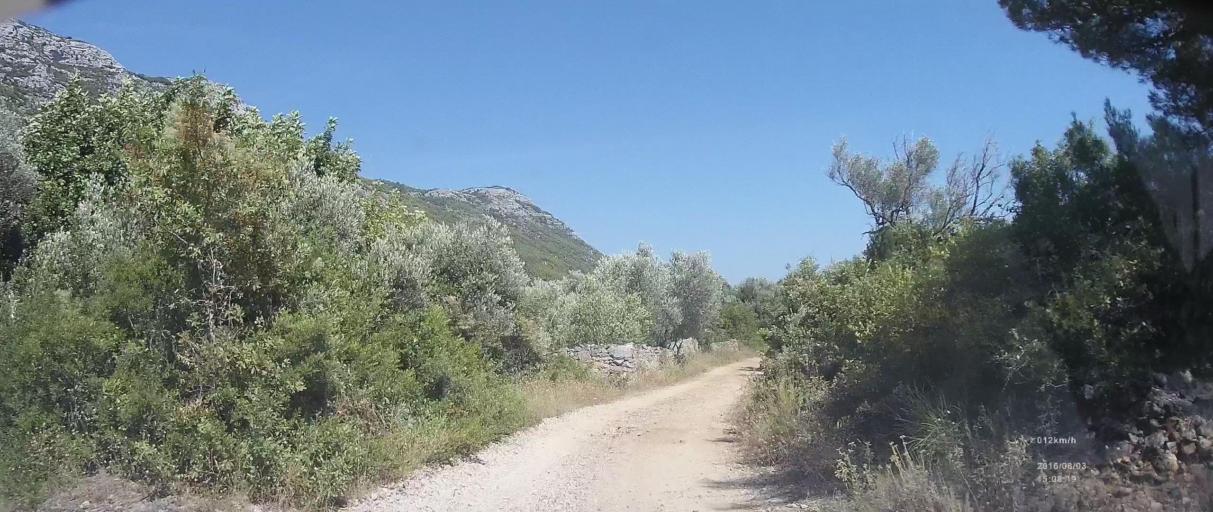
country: HR
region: Dubrovacko-Neretvanska
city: Blato
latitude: 42.7317
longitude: 17.5471
